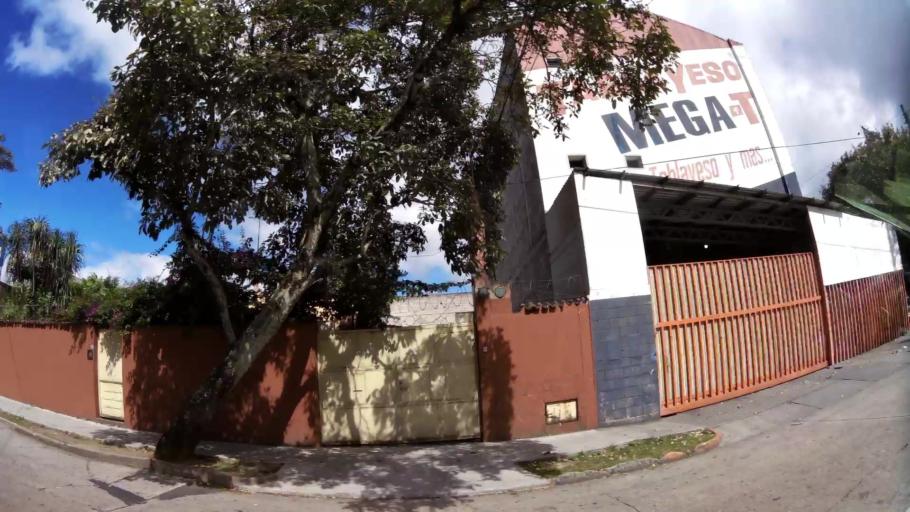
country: GT
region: Guatemala
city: Santa Catarina Pinula
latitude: 14.5987
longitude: -90.5214
